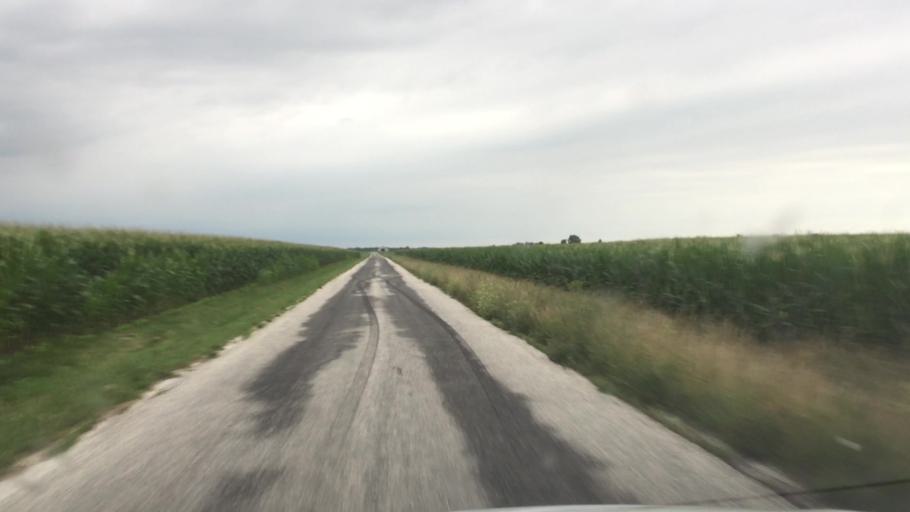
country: US
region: Illinois
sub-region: Adams County
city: Camp Point
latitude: 40.2199
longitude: -90.9691
